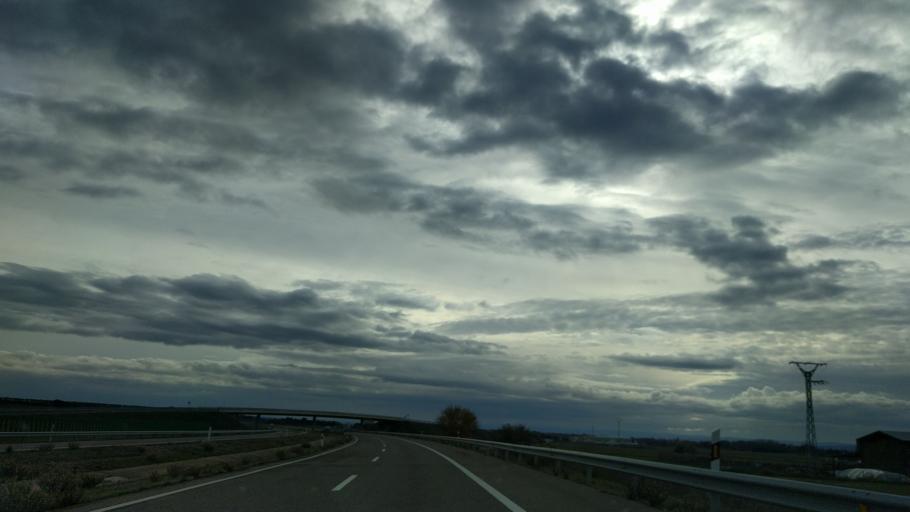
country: ES
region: Aragon
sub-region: Provincia de Huesca
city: Igries
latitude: 42.1951
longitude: -0.4362
